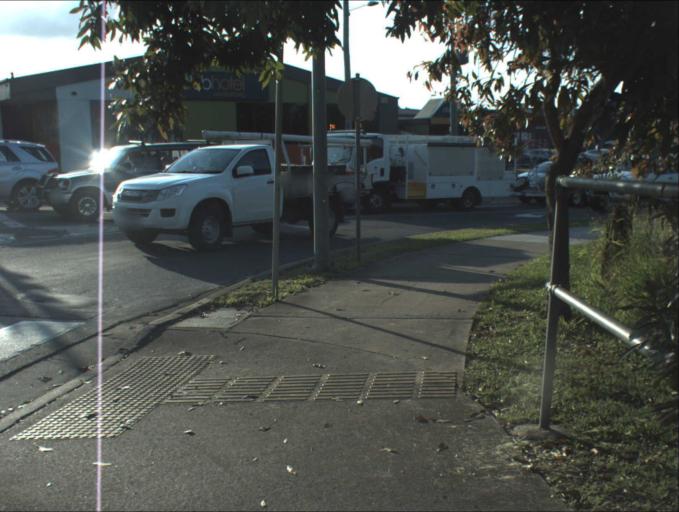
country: AU
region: Queensland
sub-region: Logan
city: Waterford West
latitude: -27.6919
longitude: 153.1365
